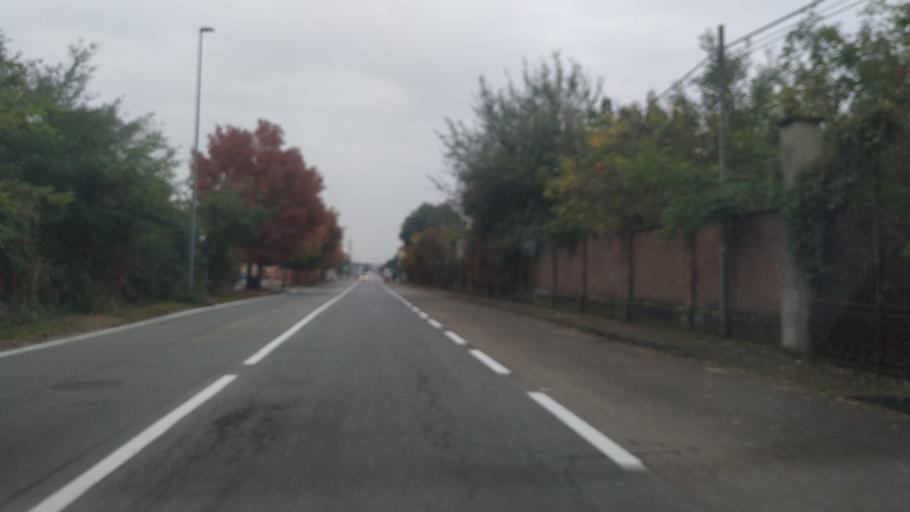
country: IT
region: Piedmont
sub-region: Provincia di Vercelli
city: Vercelli
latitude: 45.3339
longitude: 8.4181
